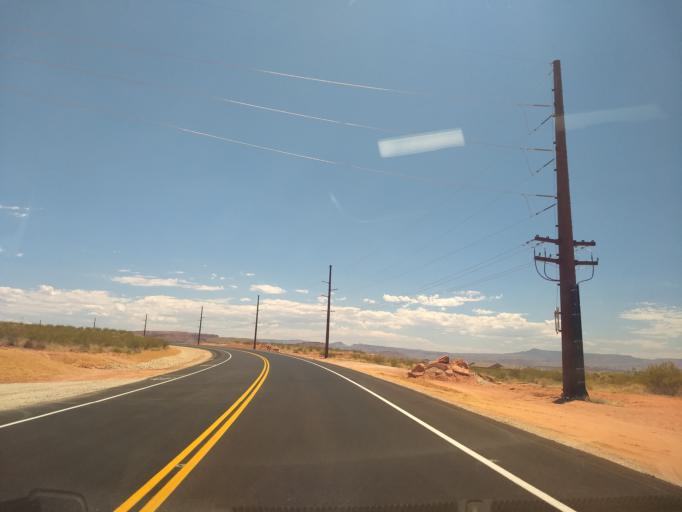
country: US
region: Utah
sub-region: Washington County
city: Washington
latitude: 37.1509
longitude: -113.5169
